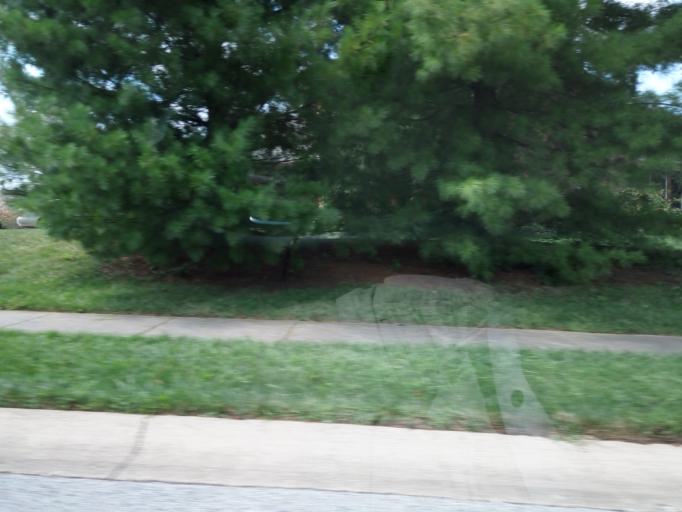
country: US
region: Kentucky
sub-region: Oldham County
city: Pewee Valley
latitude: 38.2713
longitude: -85.4807
